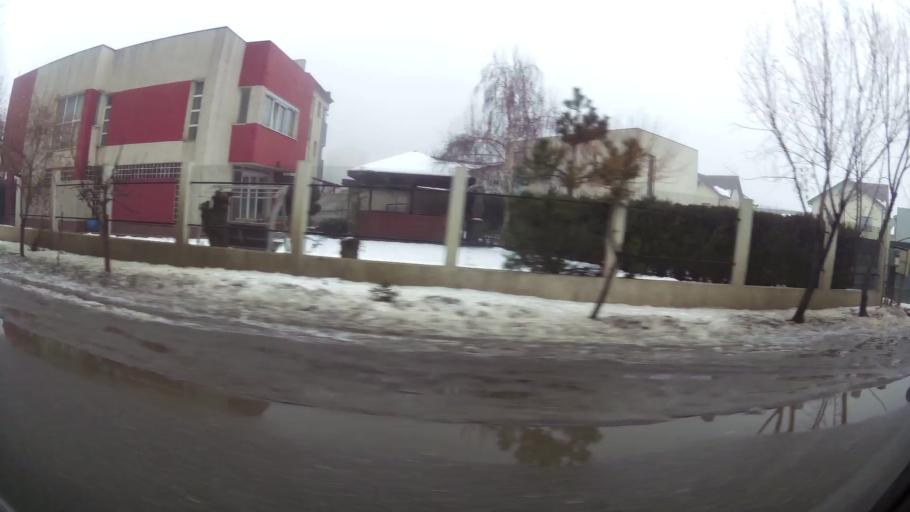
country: RO
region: Ilfov
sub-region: Comuna Chiajna
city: Chiajna
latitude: 44.4494
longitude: 25.9852
